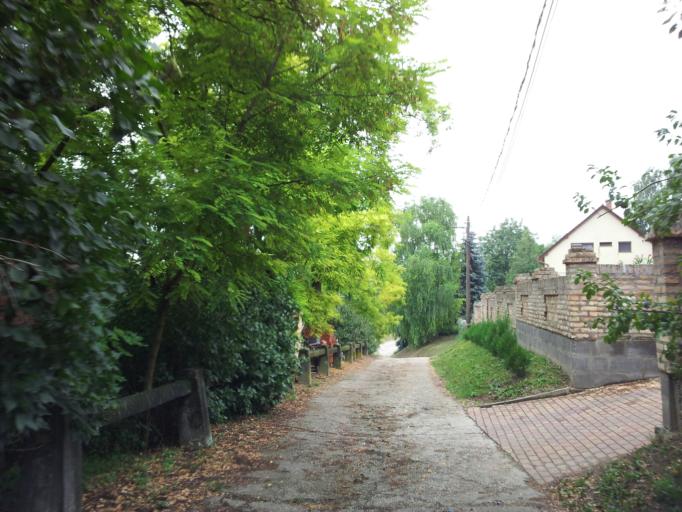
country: HU
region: Tolna
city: Tamasi
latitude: 46.6230
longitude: 18.2899
